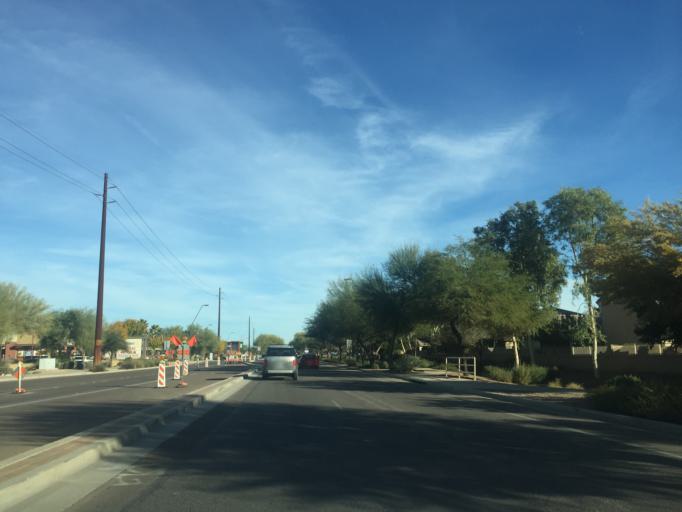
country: US
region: Arizona
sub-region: Maricopa County
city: Queen Creek
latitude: 33.2486
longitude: -111.6300
